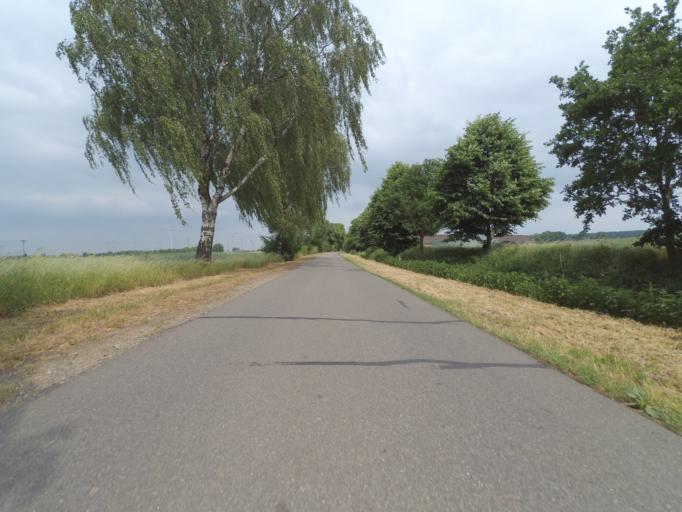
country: DE
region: Mecklenburg-Vorpommern
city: Plau am See
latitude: 53.4264
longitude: 12.1570
